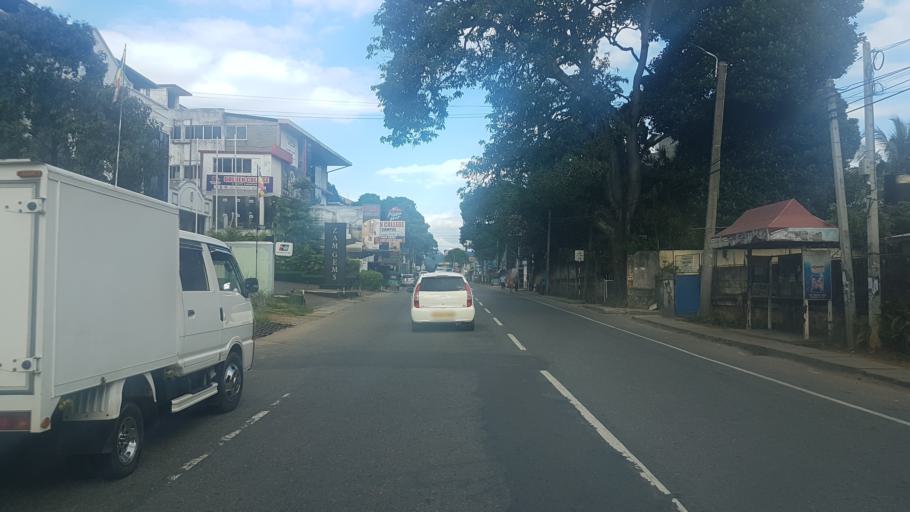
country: LK
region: Central
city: Kandy
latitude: 7.2799
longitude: 80.6188
